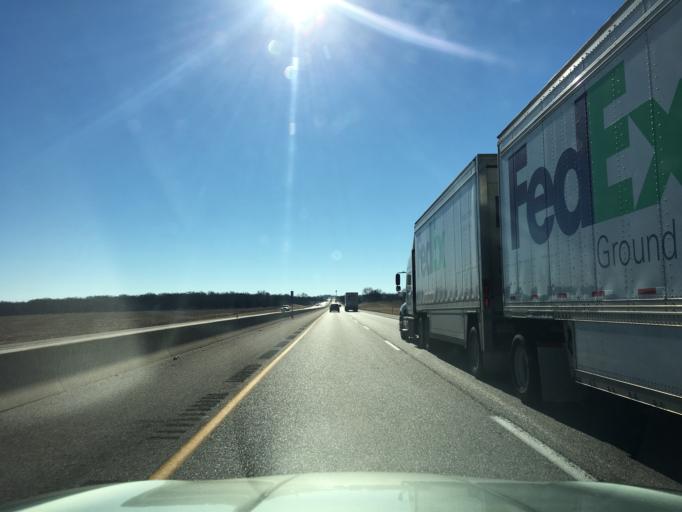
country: US
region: Kansas
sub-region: Sumner County
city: Belle Plaine
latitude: 37.3916
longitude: -97.3256
